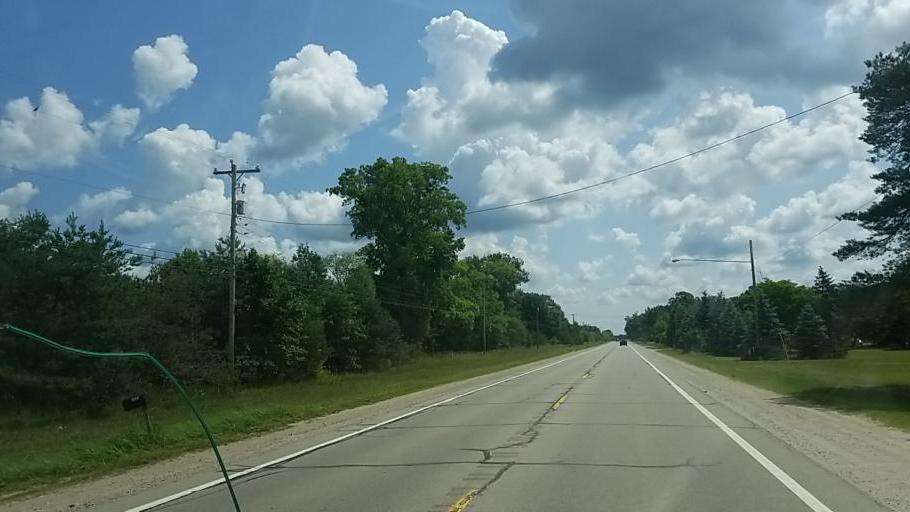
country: US
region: Michigan
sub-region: Muskegon County
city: Wolf Lake
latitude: 43.2352
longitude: -86.0461
